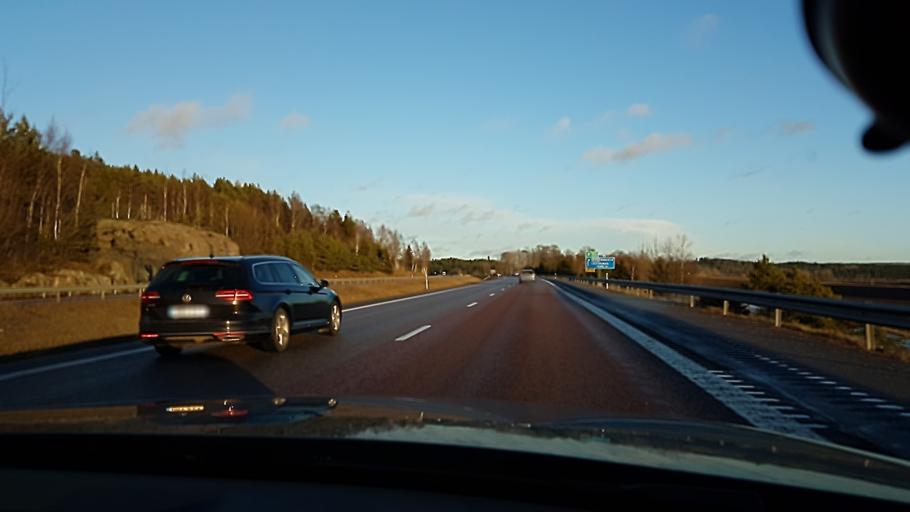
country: SE
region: Soedermanland
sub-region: Gnesta Kommun
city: Gnesta
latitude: 58.8996
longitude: 17.3022
